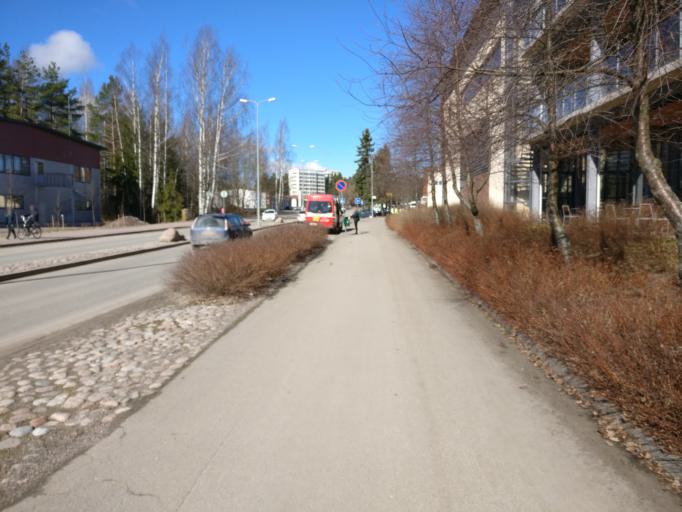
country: FI
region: Uusimaa
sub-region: Helsinki
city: Jaervenpaeae
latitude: 60.4805
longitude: 25.0815
